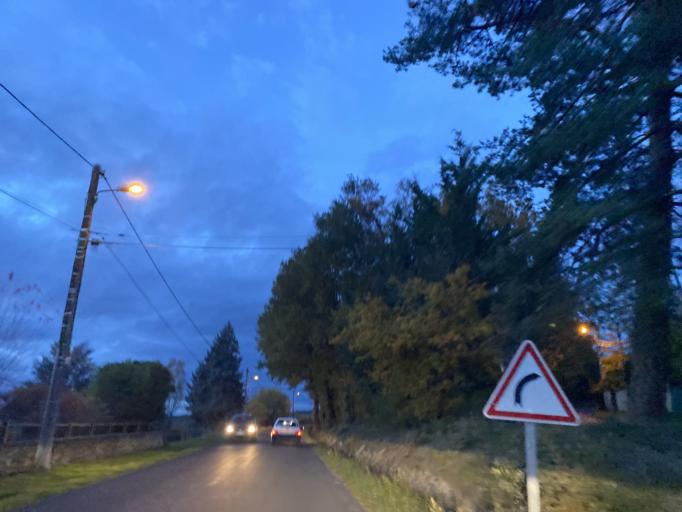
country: FR
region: Auvergne
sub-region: Departement du Puy-de-Dome
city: Peschadoires
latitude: 45.8343
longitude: 3.5210
